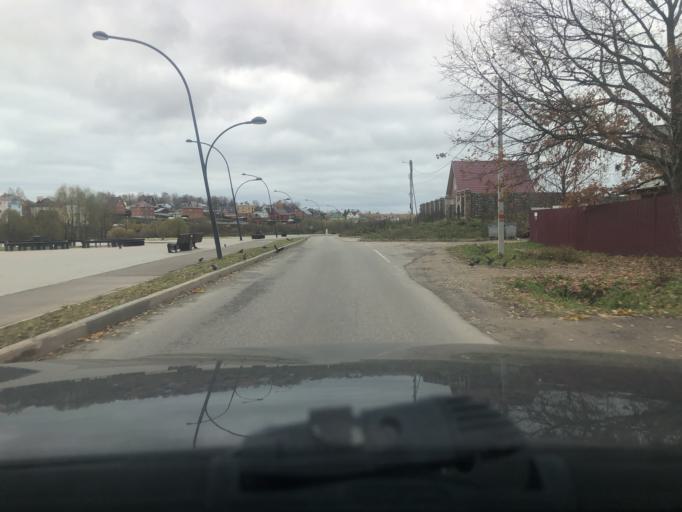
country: RU
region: Moskovskaya
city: Sergiyev Posad
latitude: 56.3024
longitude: 38.1168
